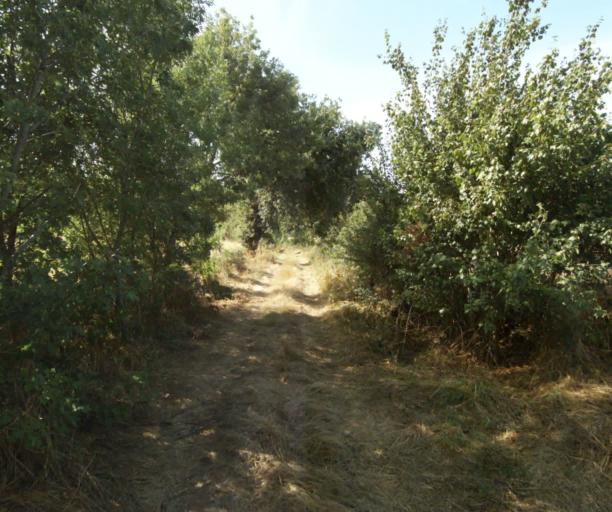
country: FR
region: Midi-Pyrenees
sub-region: Departement du Tarn
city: Soual
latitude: 43.5289
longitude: 2.0784
